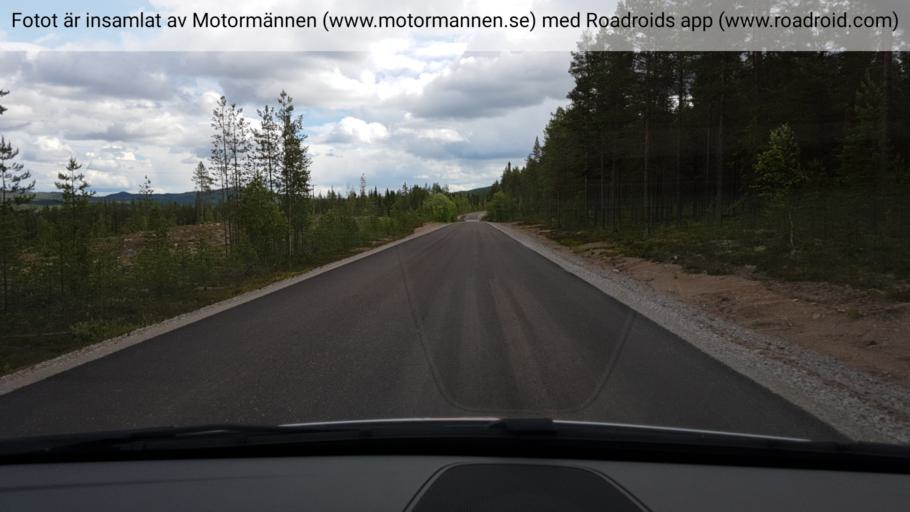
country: SE
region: Jaemtland
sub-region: Harjedalens Kommun
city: Sveg
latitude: 61.7002
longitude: 14.1840
